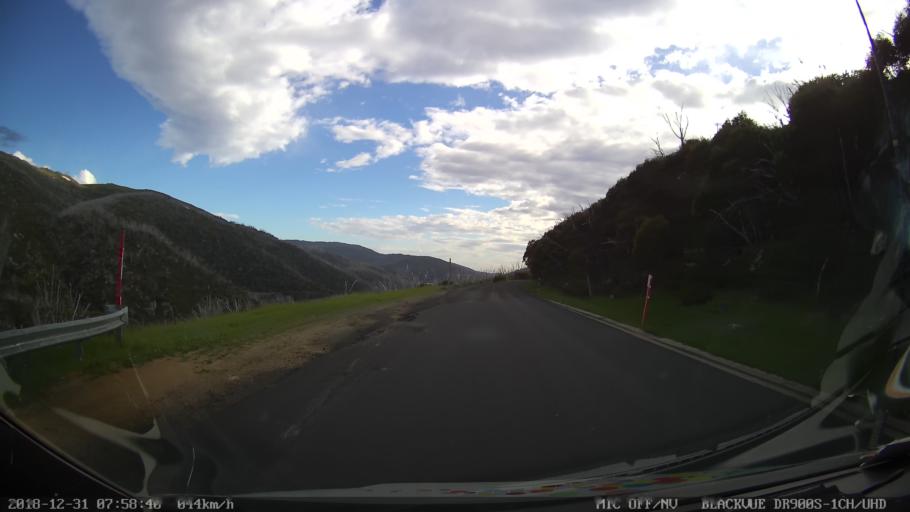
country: AU
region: New South Wales
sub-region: Snowy River
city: Jindabyne
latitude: -36.3737
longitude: 148.3806
